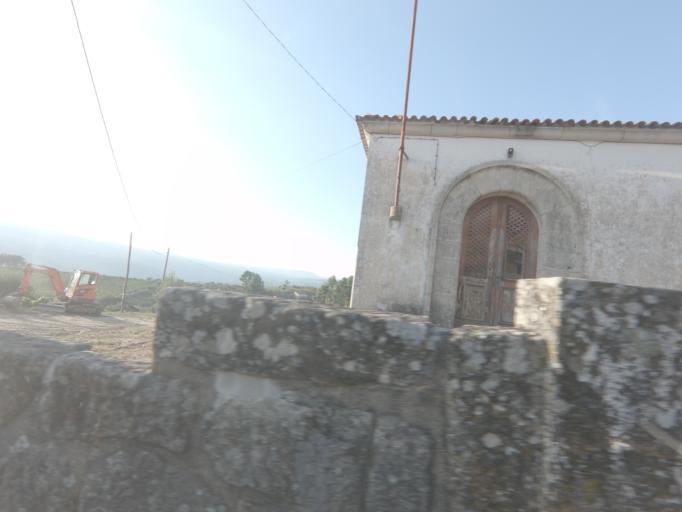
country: PT
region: Vila Real
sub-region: Sabrosa
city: Sabrosa
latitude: 41.2715
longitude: -7.5274
